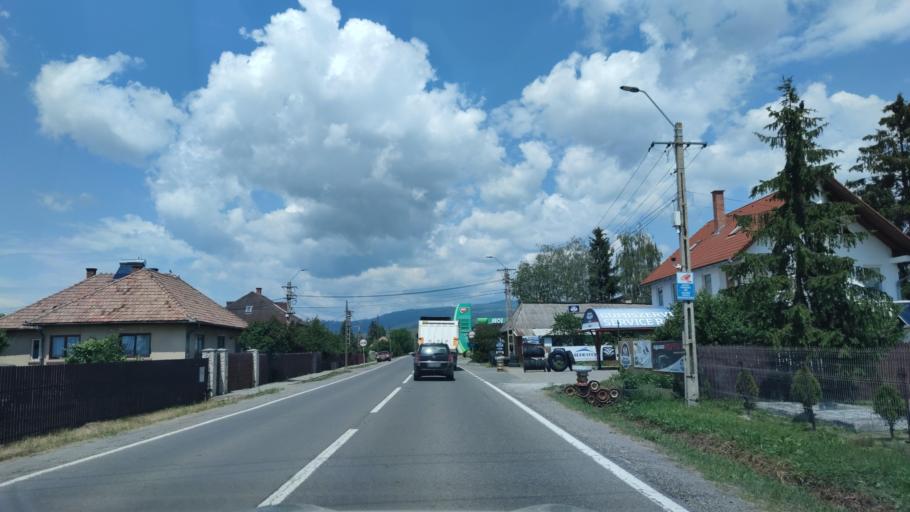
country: RO
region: Harghita
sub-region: Municipiul Gheorgheni
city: Gheorgheni
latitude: 46.7135
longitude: 25.6024
